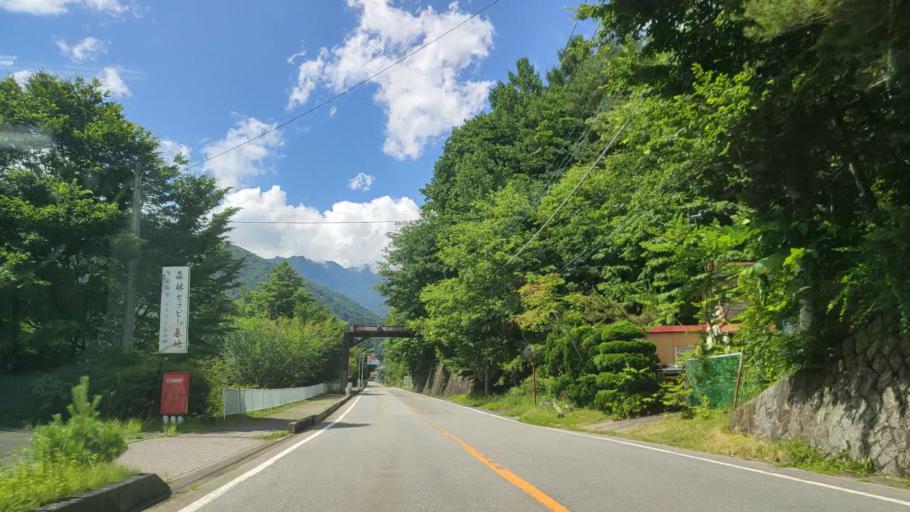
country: JP
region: Yamanashi
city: Enzan
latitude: 35.8444
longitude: 138.7636
